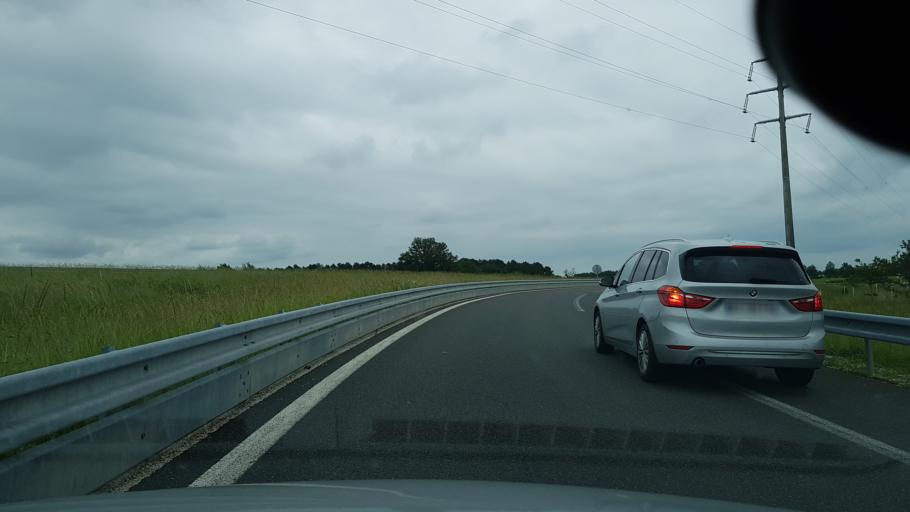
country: FR
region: Centre
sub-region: Departement du Loir-et-Cher
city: Chatillon-sur-Cher
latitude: 47.3277
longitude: 1.4988
